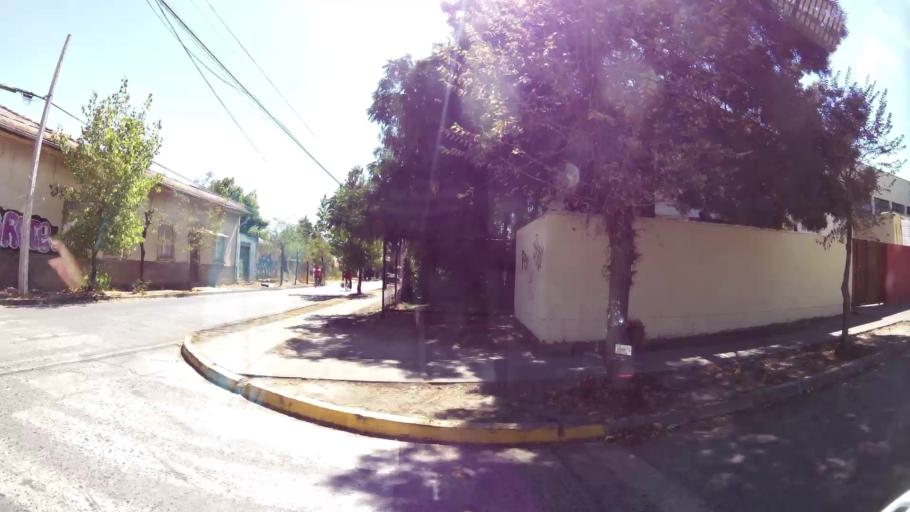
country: CL
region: O'Higgins
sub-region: Provincia de Colchagua
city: Chimbarongo
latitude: -34.5846
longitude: -70.9933
